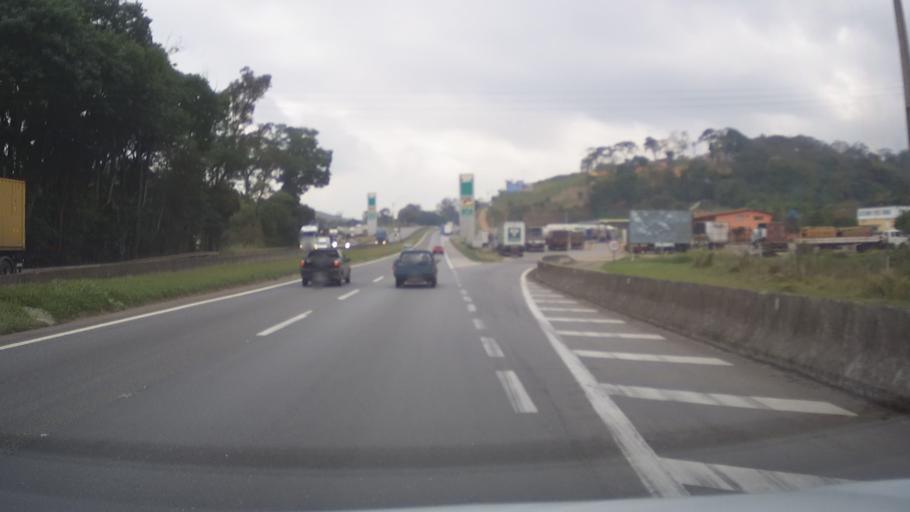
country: BR
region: Minas Gerais
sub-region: Extrema
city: Extrema
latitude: -22.8793
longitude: -46.3727
